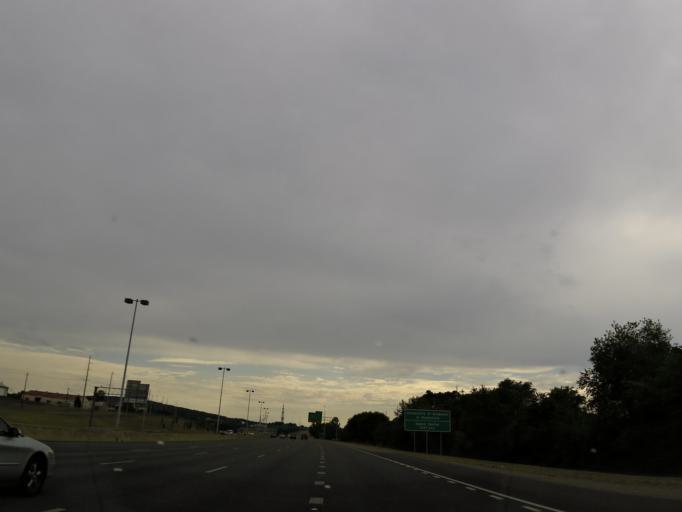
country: US
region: Alabama
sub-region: Madison County
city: Redstone Arsenal
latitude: 34.7184
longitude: -86.6346
